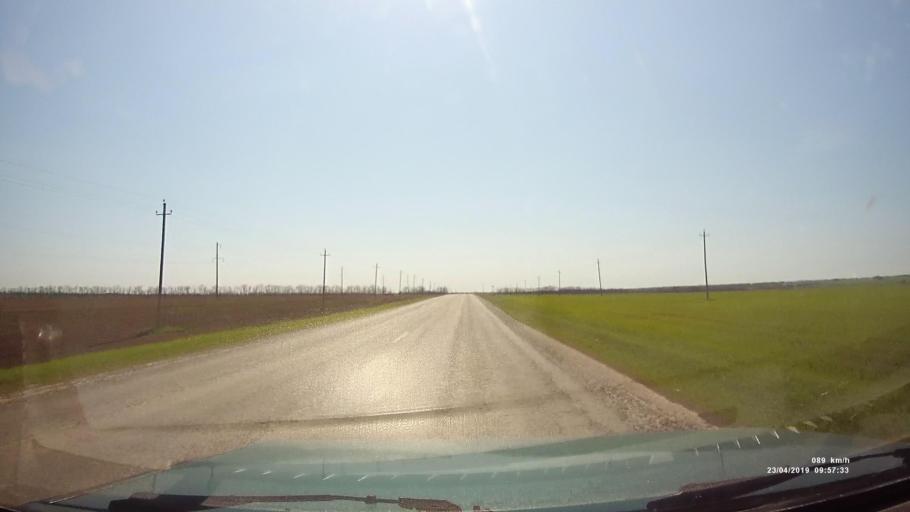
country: RU
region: Rostov
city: Orlovskiy
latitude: 46.7879
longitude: 42.0870
